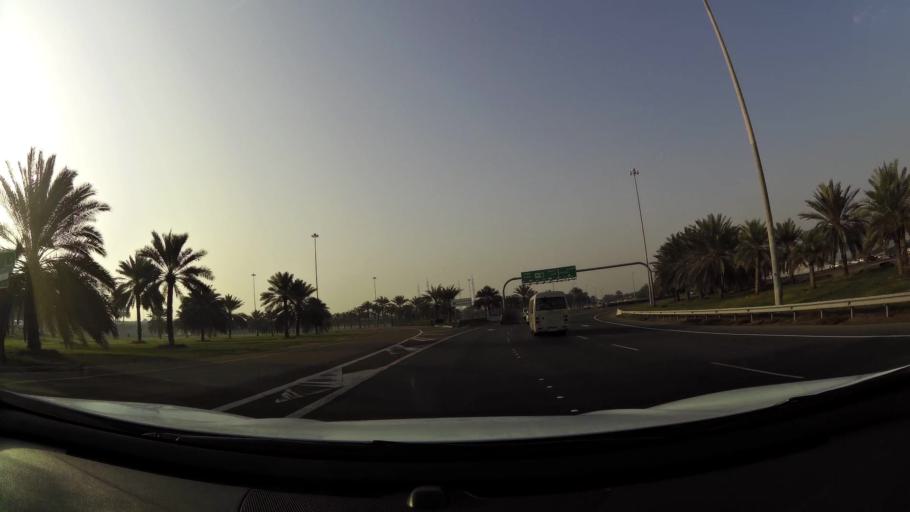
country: AE
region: Abu Dhabi
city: Abu Dhabi
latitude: 24.4234
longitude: 54.4754
